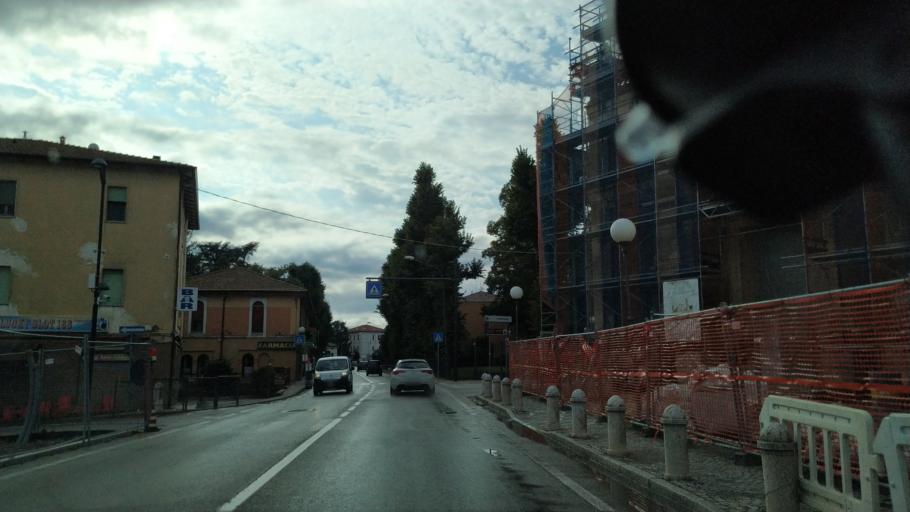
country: IT
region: Emilia-Romagna
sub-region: Provincia di Ferrara
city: Sant'Agostino
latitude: 44.7925
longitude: 11.3867
